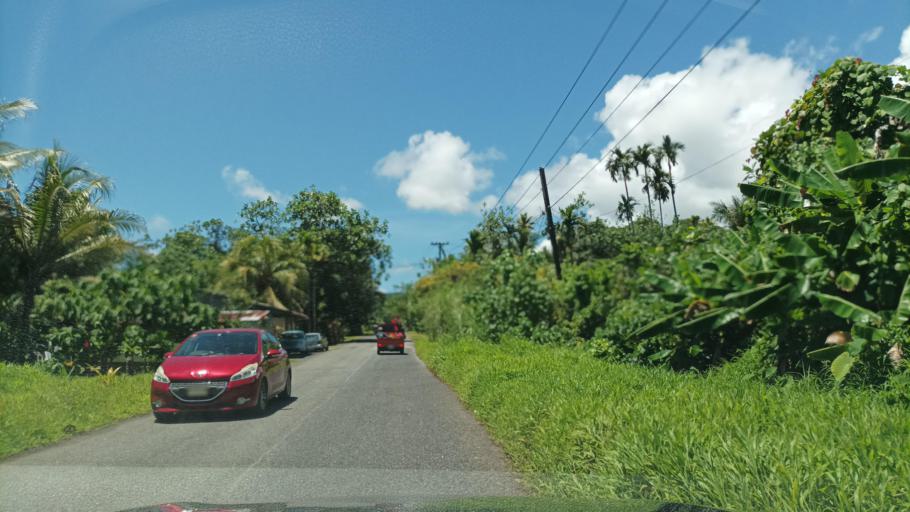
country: FM
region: Pohnpei
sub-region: Kolonia Municipality
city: Kolonia
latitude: 6.9443
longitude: 158.2748
